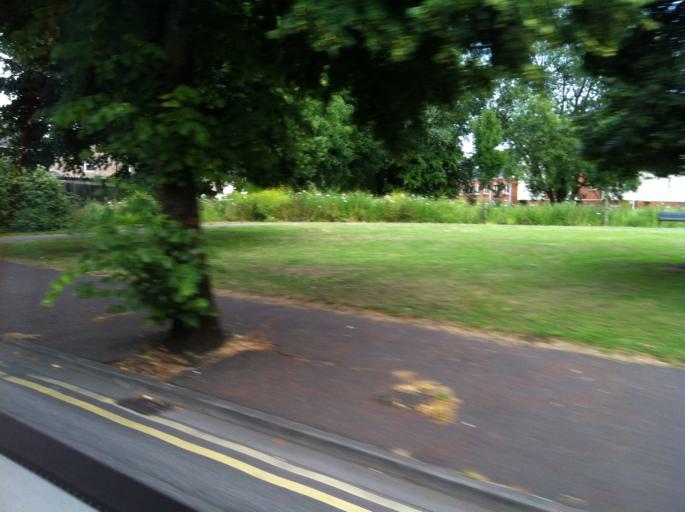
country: GB
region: Wales
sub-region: Cardiff
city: Cardiff
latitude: 51.4630
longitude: -3.1823
